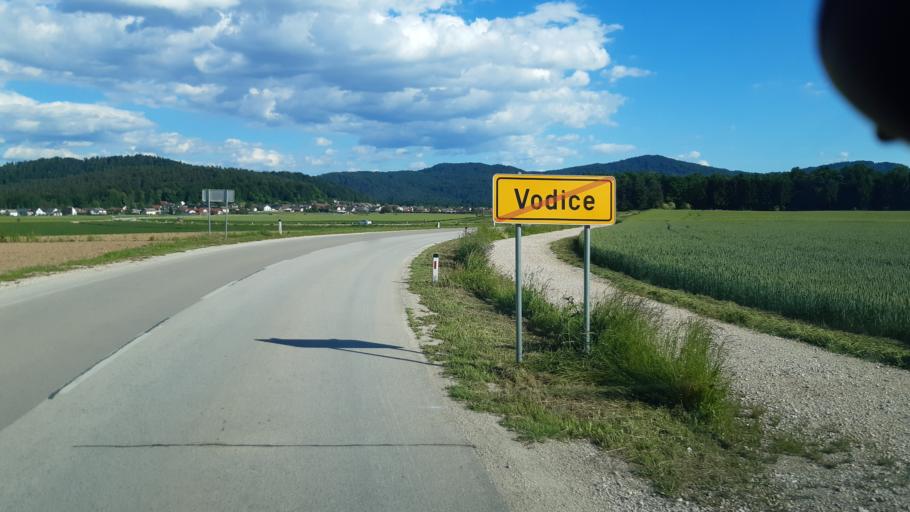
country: SI
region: Vodice
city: Vodice
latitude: 46.1843
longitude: 14.4965
